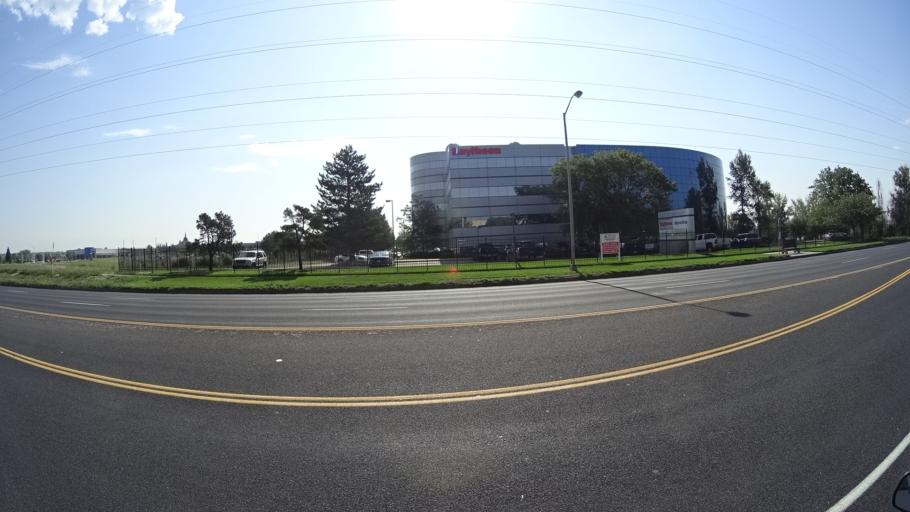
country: US
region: Colorado
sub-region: El Paso County
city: Stratmoor
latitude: 38.8151
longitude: -104.7577
